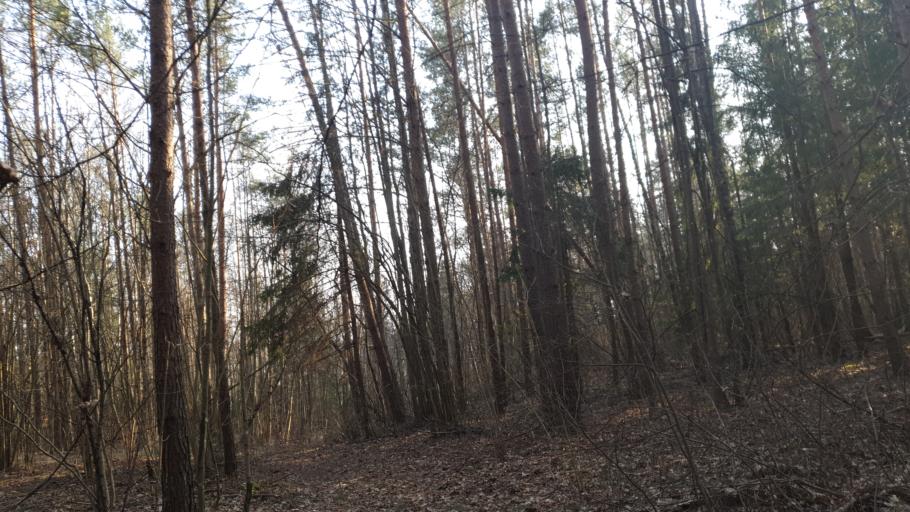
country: LT
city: Nemencine
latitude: 54.8733
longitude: 25.5712
